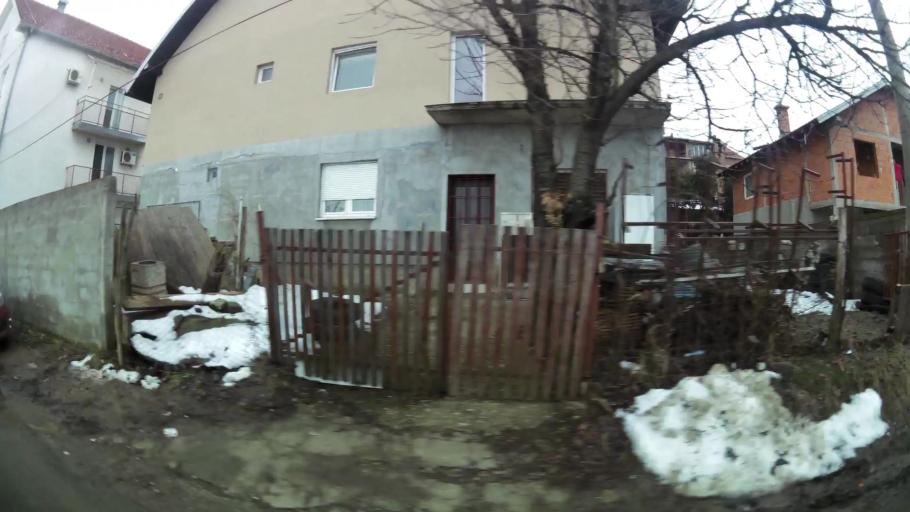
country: RS
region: Central Serbia
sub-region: Belgrade
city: Cukarica
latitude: 44.7464
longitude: 20.3988
